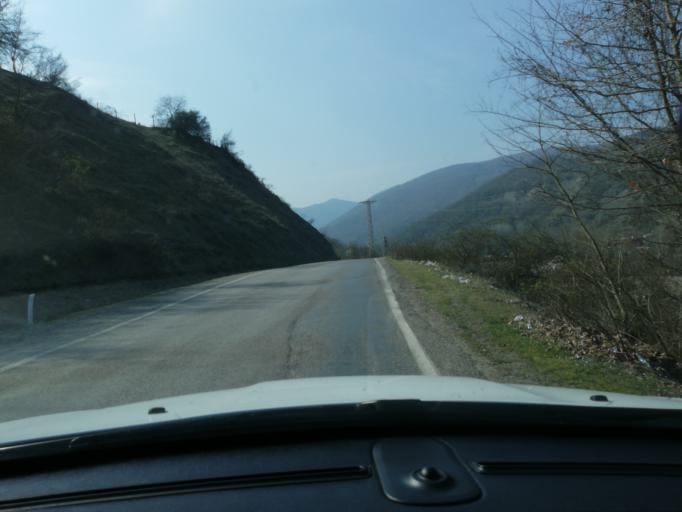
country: TR
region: Karabuk
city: Yenice
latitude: 41.2330
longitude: 32.3606
